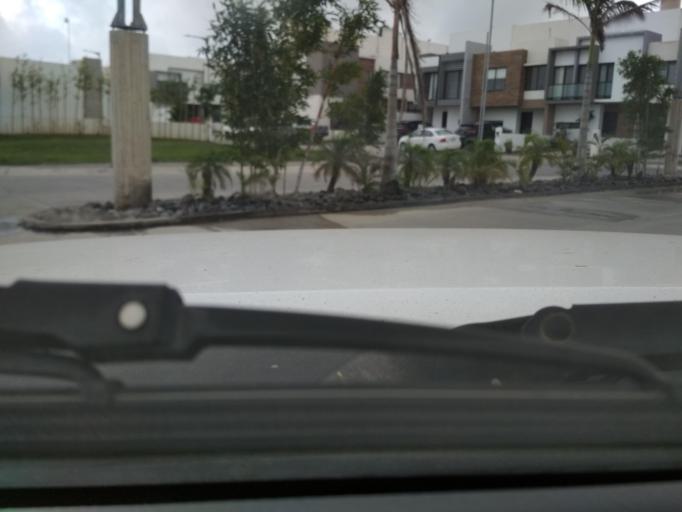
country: MX
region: Veracruz
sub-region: Veracruz
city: Fraccionamiento Geovillas los Pinos
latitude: 19.2167
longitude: -96.2323
